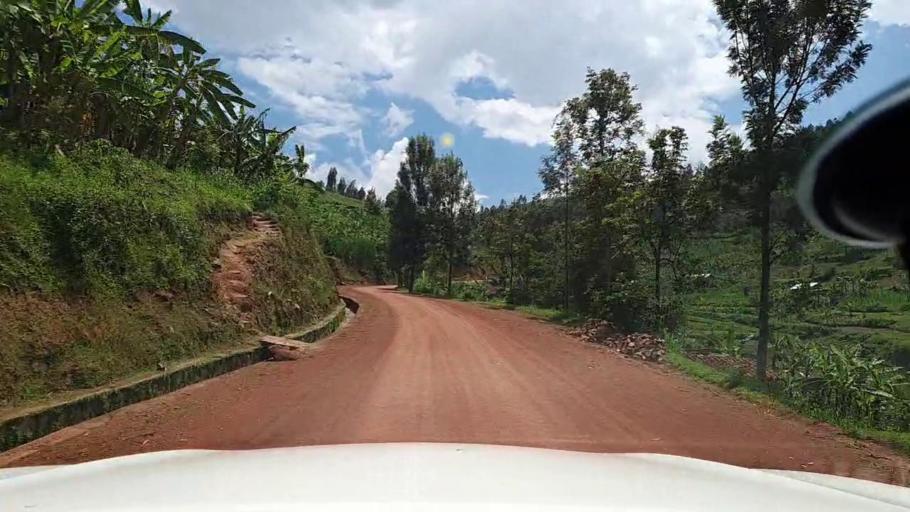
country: RW
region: Northern Province
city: Byumba
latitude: -1.7517
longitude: 29.8505
